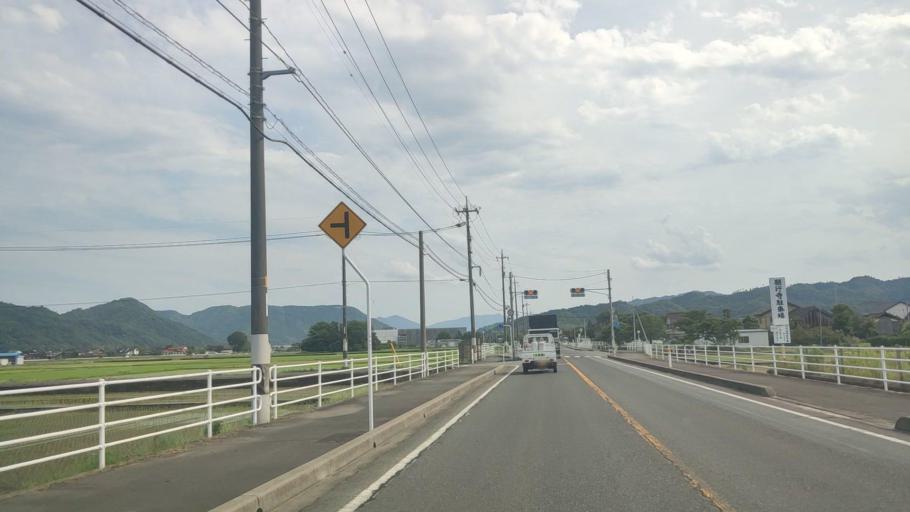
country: JP
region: Tottori
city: Tottori
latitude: 35.4591
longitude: 134.2036
